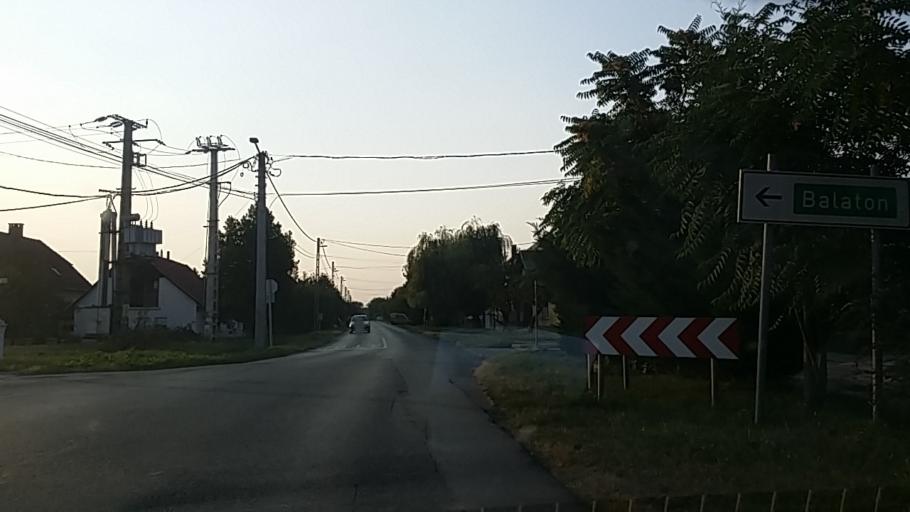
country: HU
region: Tolna
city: Dunafoldvar
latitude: 46.8143
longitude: 18.9182
